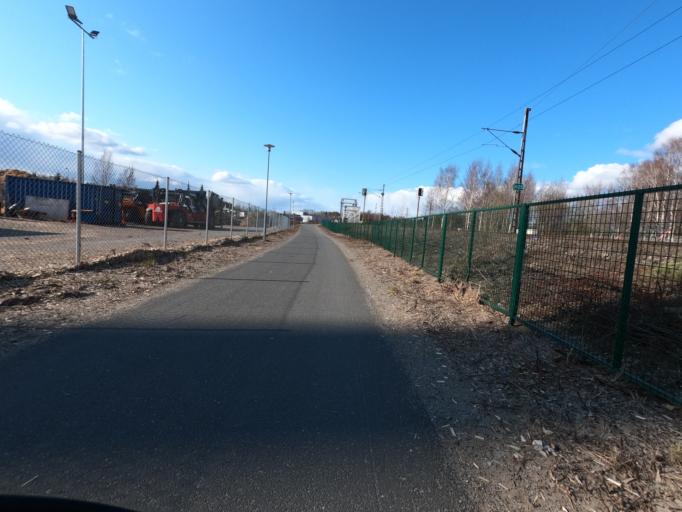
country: FI
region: North Karelia
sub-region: Joensuu
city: Joensuu
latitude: 62.6049
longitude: 29.7803
